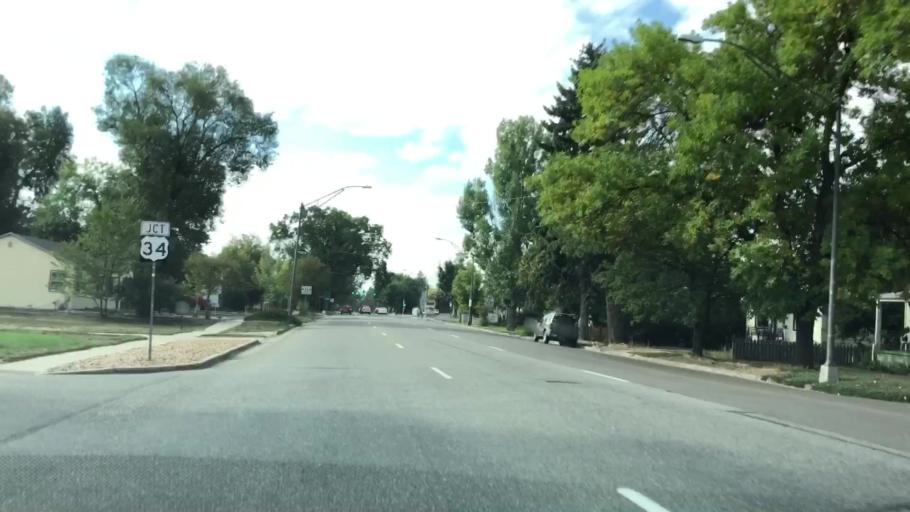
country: US
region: Colorado
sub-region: Larimer County
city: Loveland
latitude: 40.4093
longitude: -105.0744
